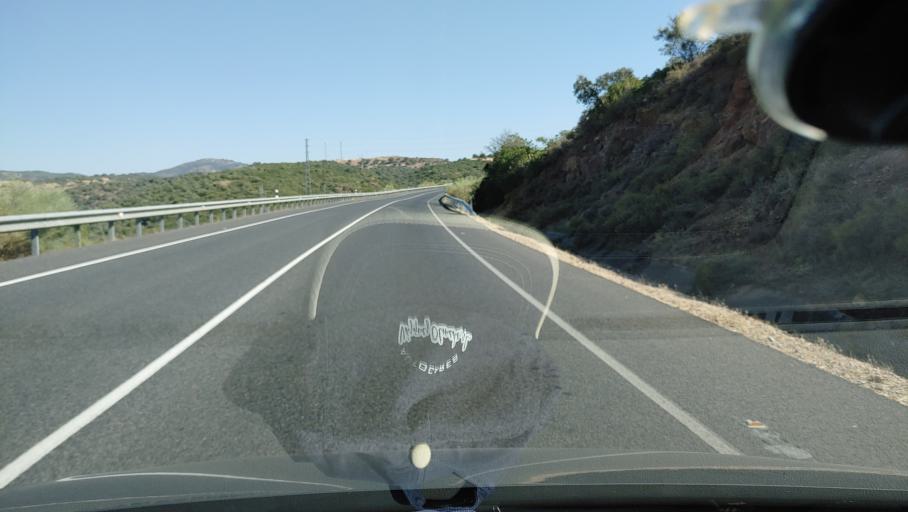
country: ES
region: Andalusia
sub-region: Province of Cordoba
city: Cordoba
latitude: 37.9290
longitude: -4.7663
